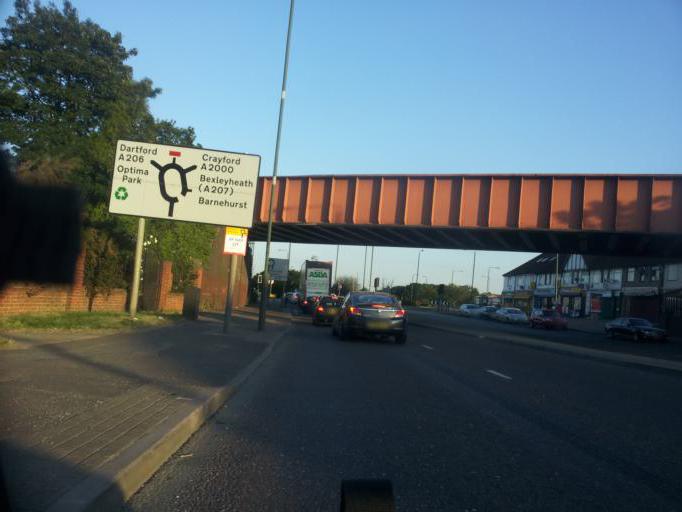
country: GB
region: England
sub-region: Greater London
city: Erith
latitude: 51.4646
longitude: 0.1818
